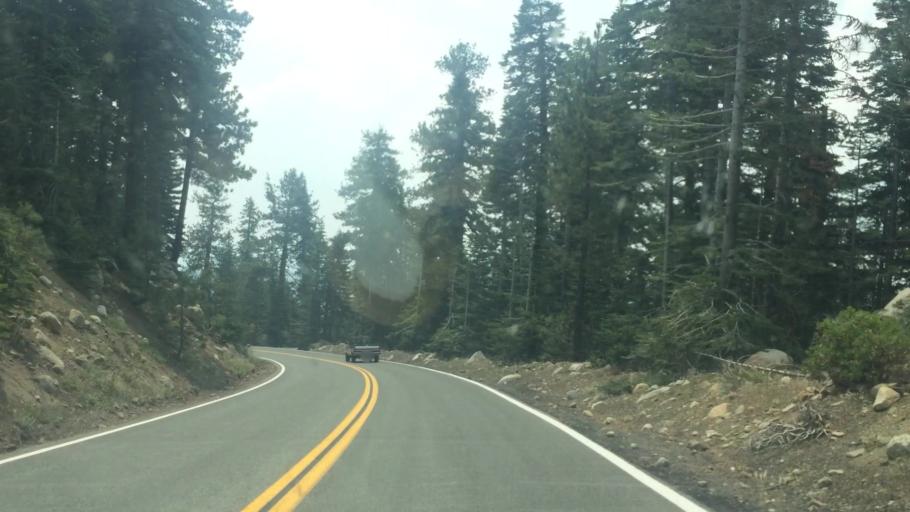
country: US
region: California
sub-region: El Dorado County
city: South Lake Tahoe
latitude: 38.6907
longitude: -120.1239
